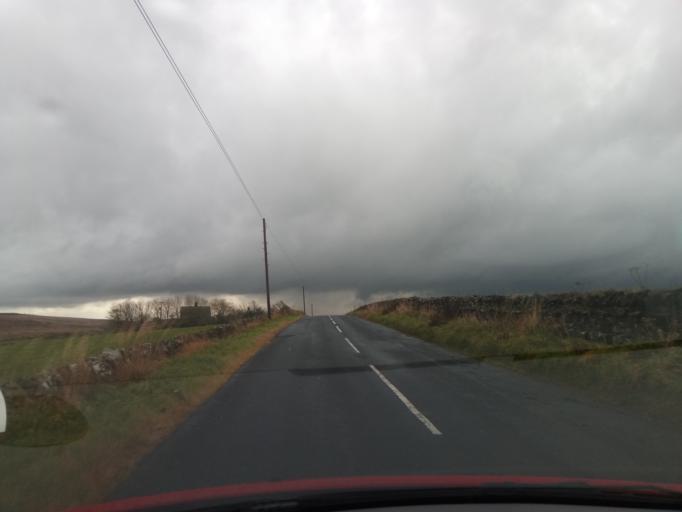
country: GB
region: England
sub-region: Northumberland
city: Corsenside
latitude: 55.1767
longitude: -2.2599
